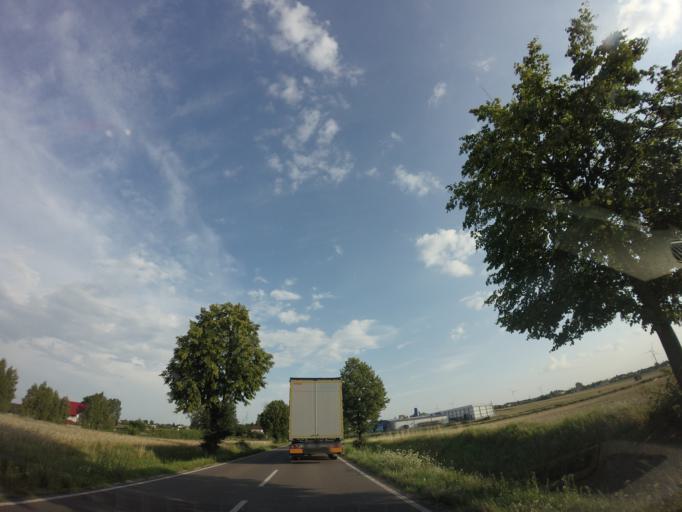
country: PL
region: Lublin Voivodeship
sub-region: Powiat lubartowski
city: Michow
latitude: 51.5315
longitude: 22.3121
